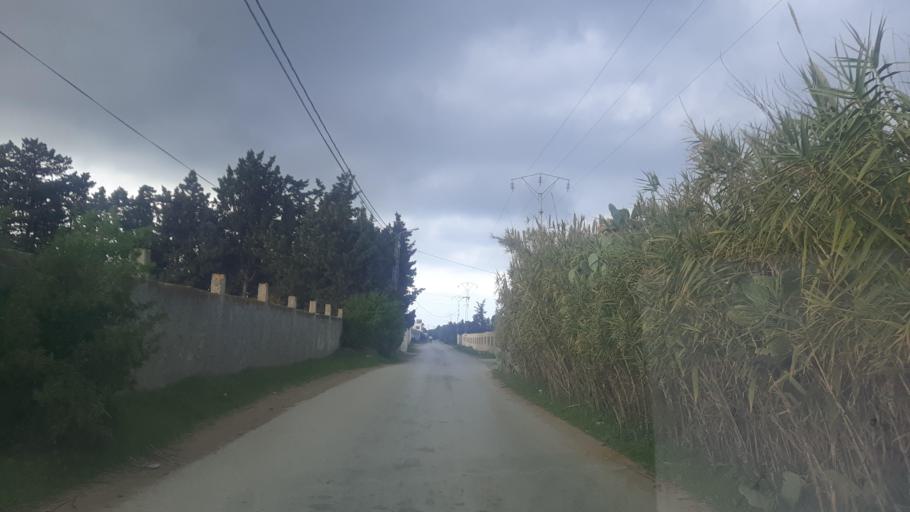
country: TN
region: Nabul
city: Manzil Bu Zalafah
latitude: 36.7314
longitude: 10.5385
